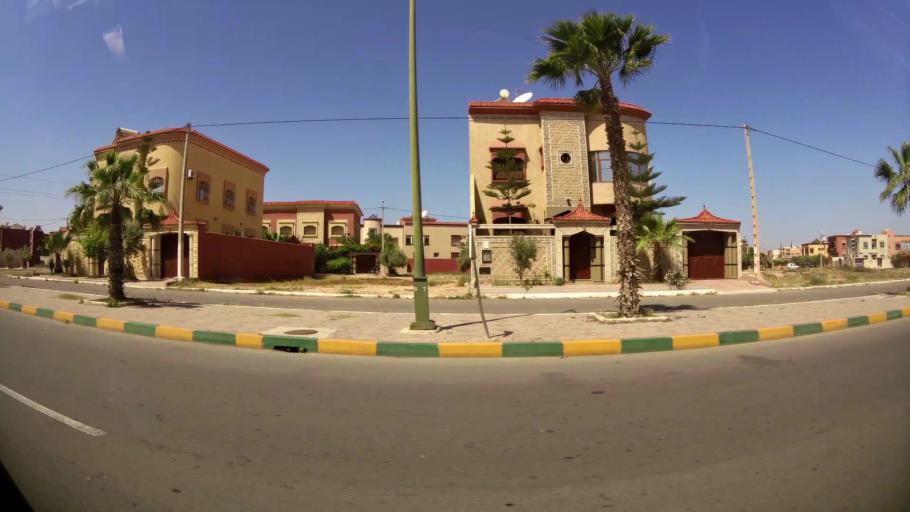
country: MA
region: Souss-Massa-Draa
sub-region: Inezgane-Ait Mellou
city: Inezgane
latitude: 30.3246
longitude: -9.5039
